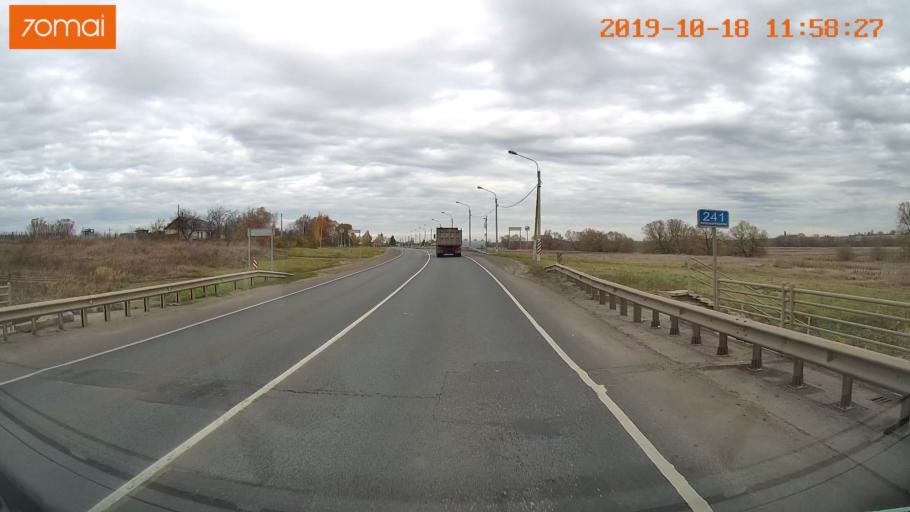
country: RU
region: Rjazan
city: Zakharovo
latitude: 54.2718
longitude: 39.1676
